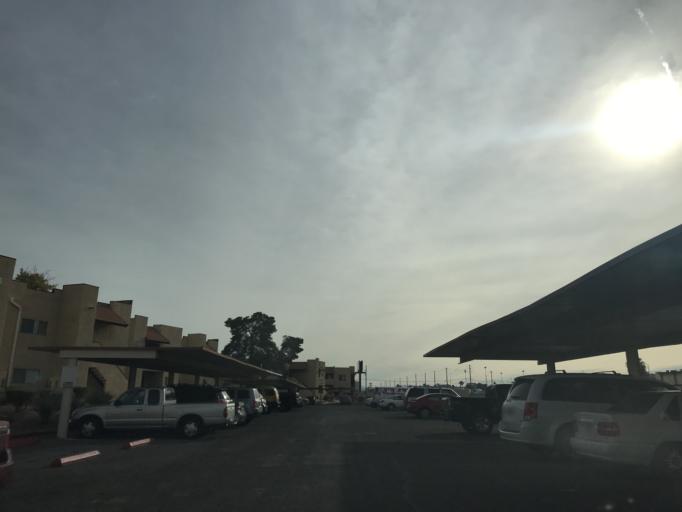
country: US
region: Nevada
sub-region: Clark County
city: Paradise
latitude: 36.0925
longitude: -115.1698
